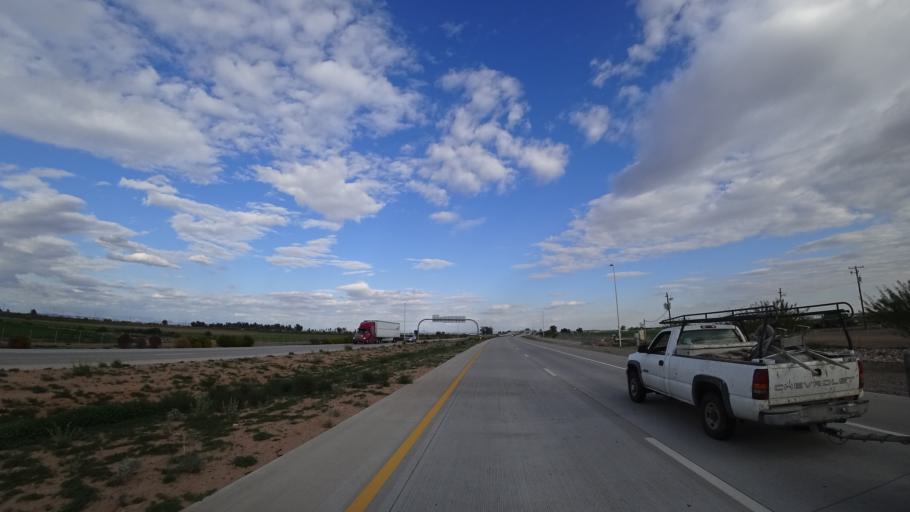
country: US
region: Arizona
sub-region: Maricopa County
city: Citrus Park
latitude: 33.5590
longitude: -112.3774
